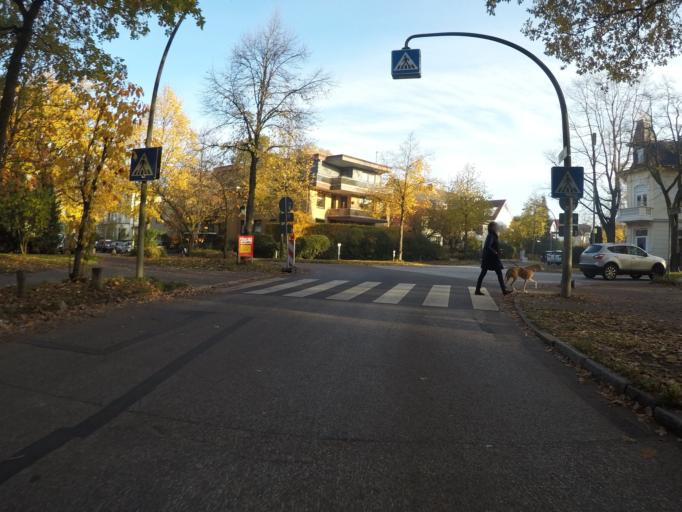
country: DE
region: Hamburg
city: Hamburg-Nord
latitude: 53.5923
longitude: 9.9608
